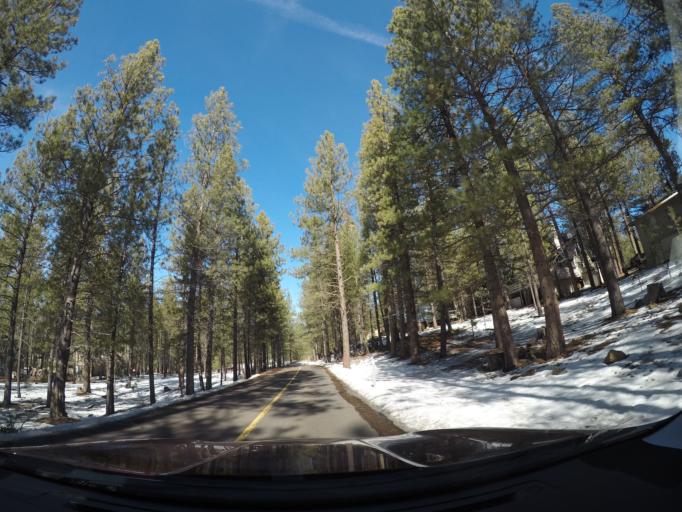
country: US
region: Oregon
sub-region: Deschutes County
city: Sunriver
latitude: 43.8761
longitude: -121.4308
